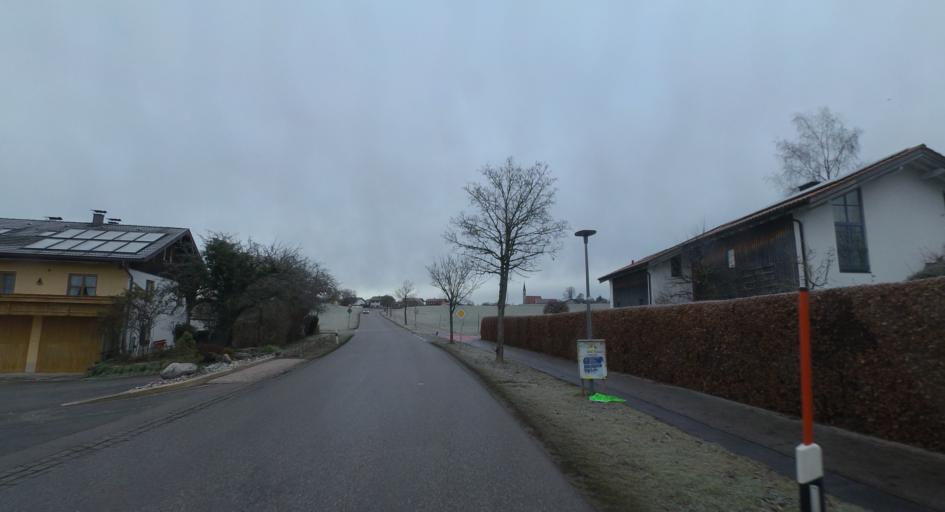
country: DE
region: Bavaria
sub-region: Upper Bavaria
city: Traunstein
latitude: 47.9178
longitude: 12.6497
